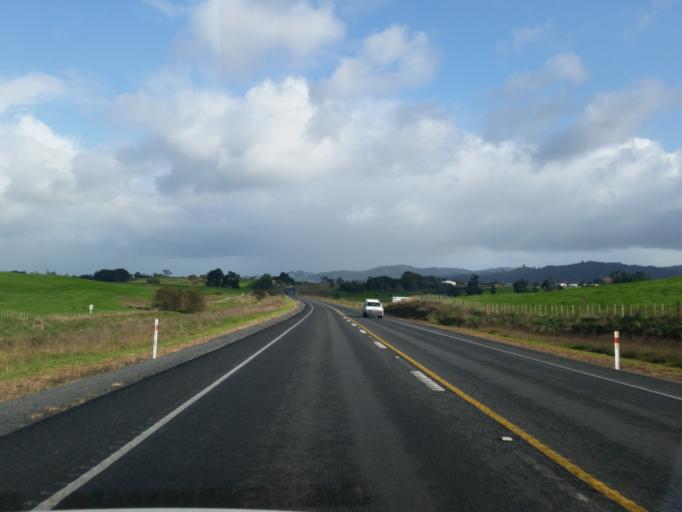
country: NZ
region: Waikato
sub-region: Waikato District
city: Te Kauwhata
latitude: -37.2208
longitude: 175.1340
